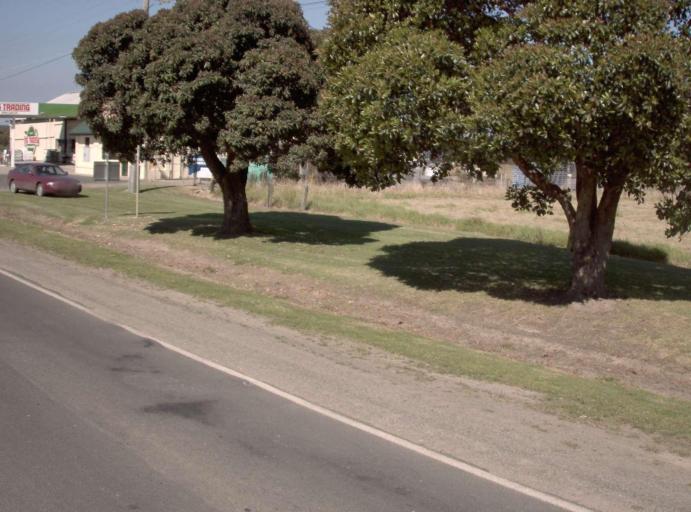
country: AU
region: Victoria
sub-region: Latrobe
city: Traralgon
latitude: -38.5533
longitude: 146.6803
